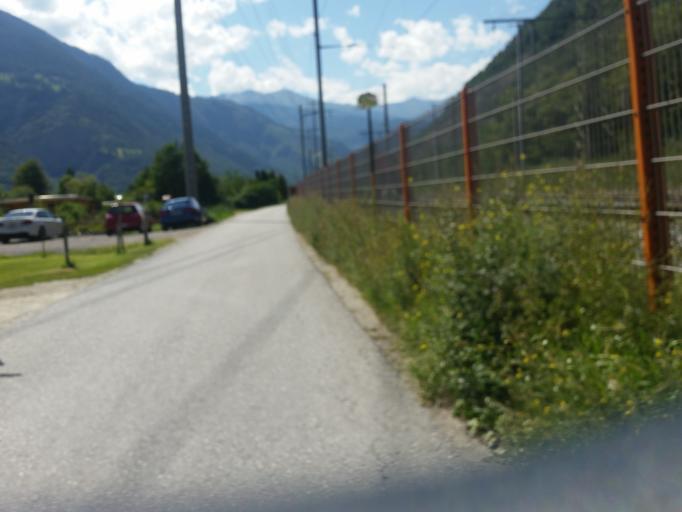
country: CH
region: Valais
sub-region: Brig District
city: Brig
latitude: 46.3163
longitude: 7.9745
